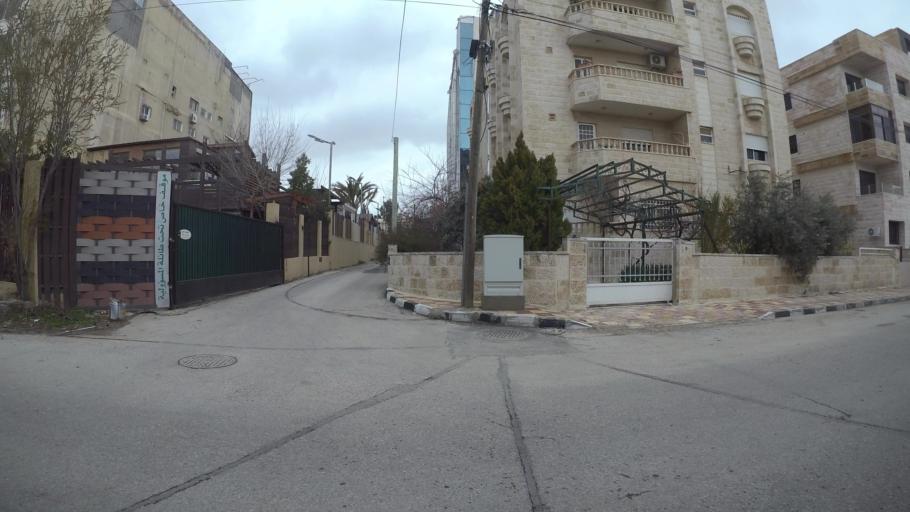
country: JO
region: Amman
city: Al Jubayhah
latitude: 31.9963
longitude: 35.8442
